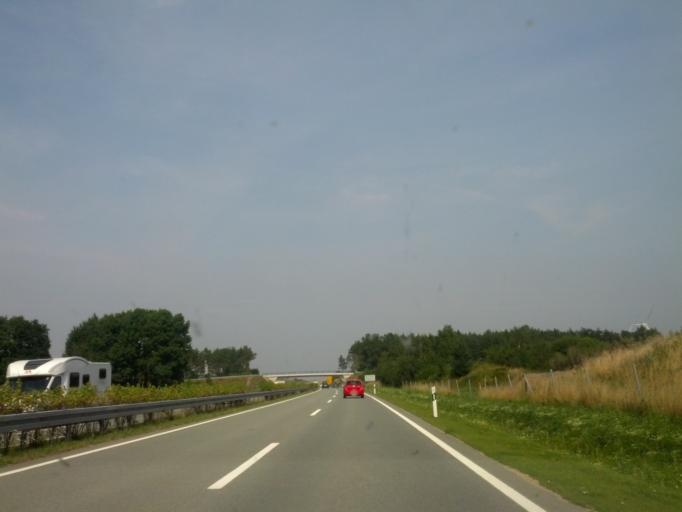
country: DE
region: Mecklenburg-Vorpommern
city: Brandshagen
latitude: 54.1572
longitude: 13.1731
